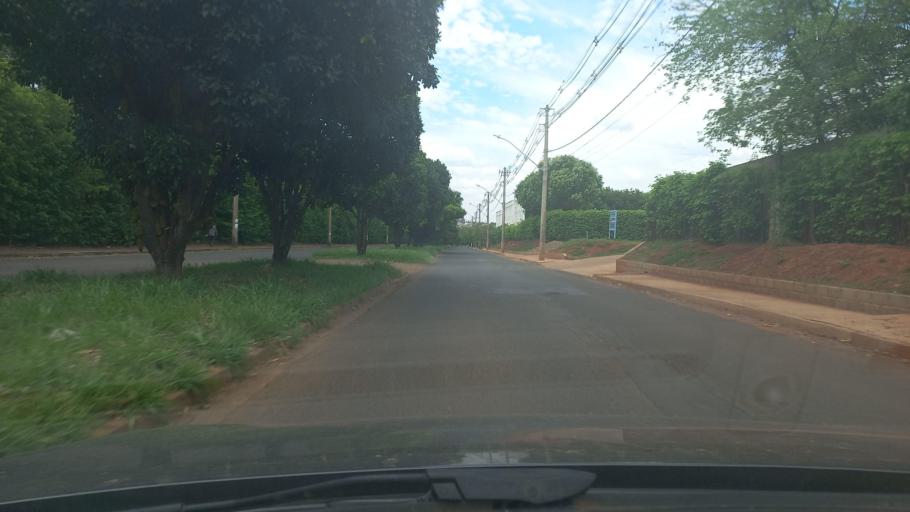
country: BR
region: Minas Gerais
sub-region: Uberaba
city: Uberaba
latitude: -19.7425
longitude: -47.9769
